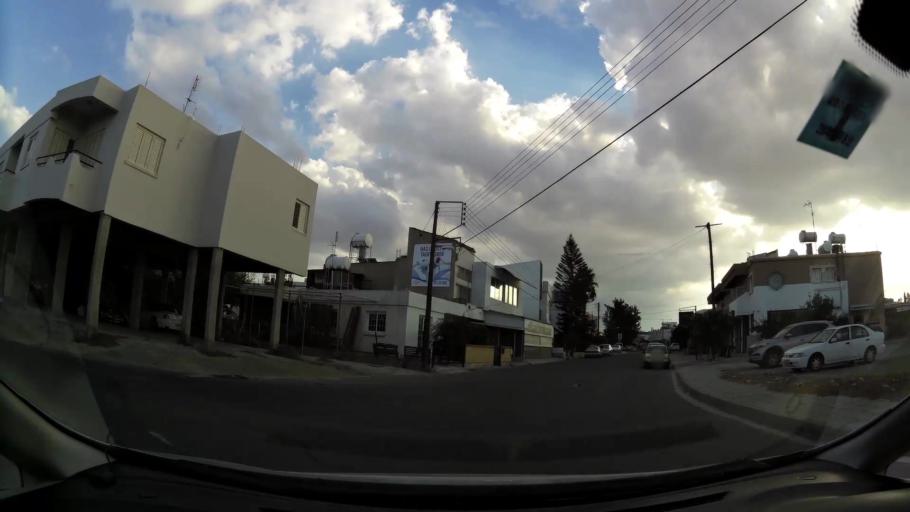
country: CY
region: Lefkosia
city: Kato Deftera
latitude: 35.1144
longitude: 33.3007
